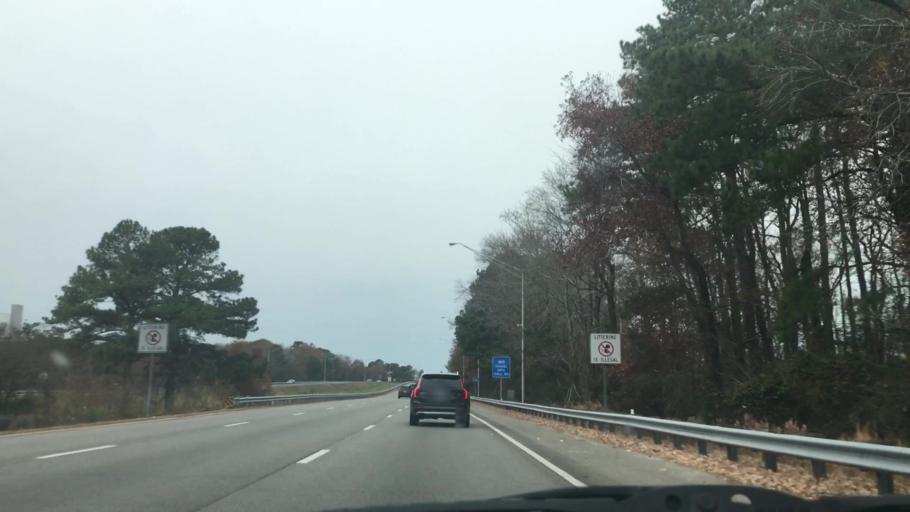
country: US
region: Virginia
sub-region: City of Virginia Beach
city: Virginia Beach
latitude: 36.8480
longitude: -75.9882
